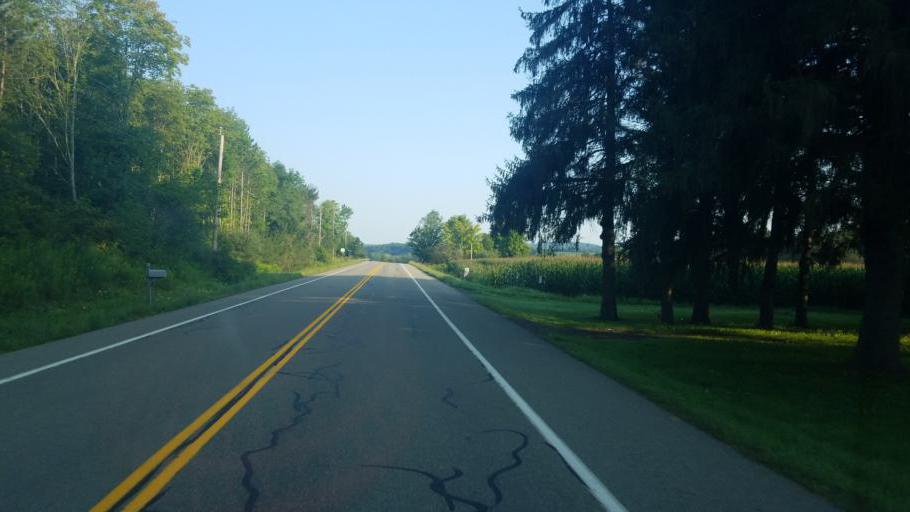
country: US
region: Pennsylvania
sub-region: Tioga County
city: Westfield
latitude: 42.0113
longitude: -77.5187
